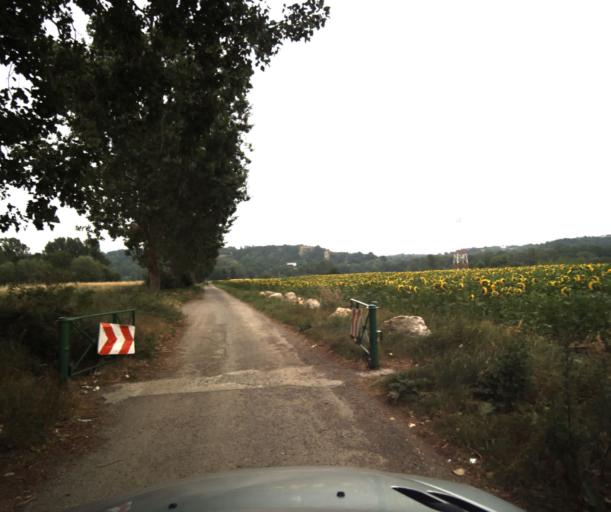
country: FR
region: Midi-Pyrenees
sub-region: Departement de la Haute-Garonne
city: Portet-sur-Garonne
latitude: 43.5308
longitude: 1.4199
